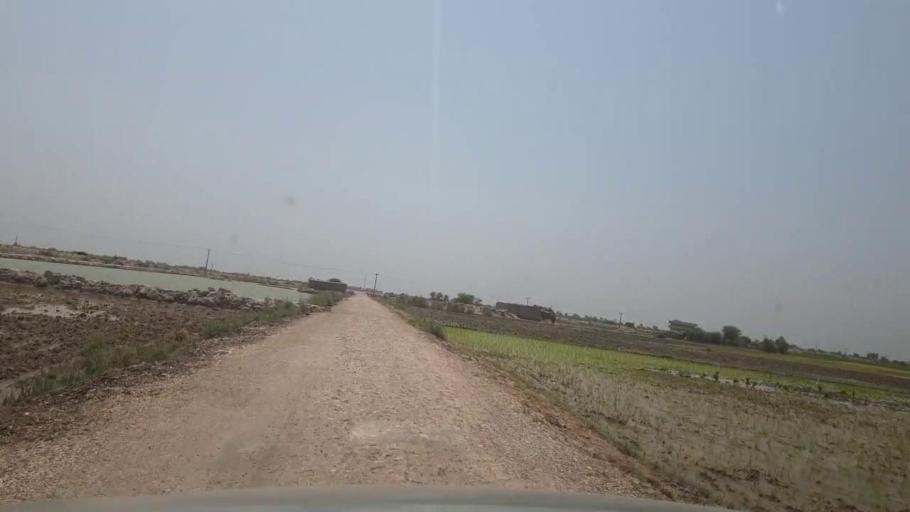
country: PK
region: Sindh
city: Lakhi
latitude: 27.8419
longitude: 68.6624
